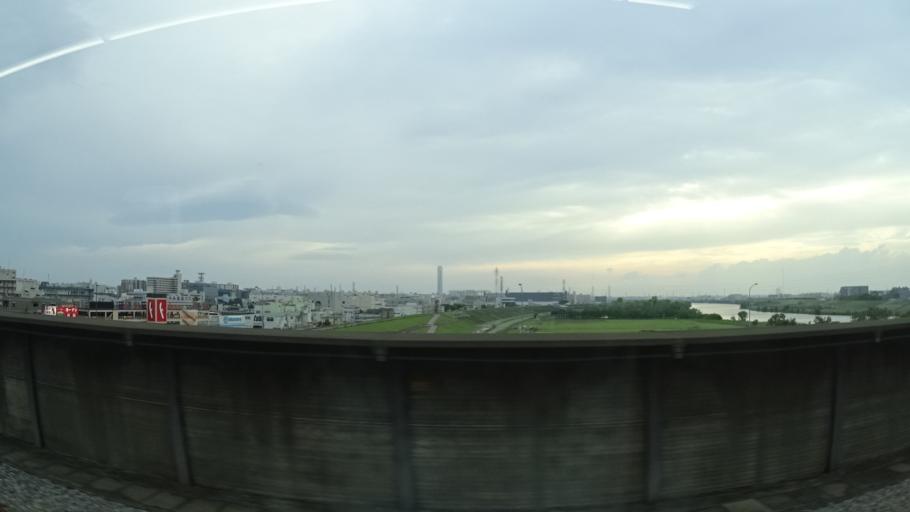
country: JP
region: Saitama
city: Shimotoda
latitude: 35.7975
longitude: 139.6859
